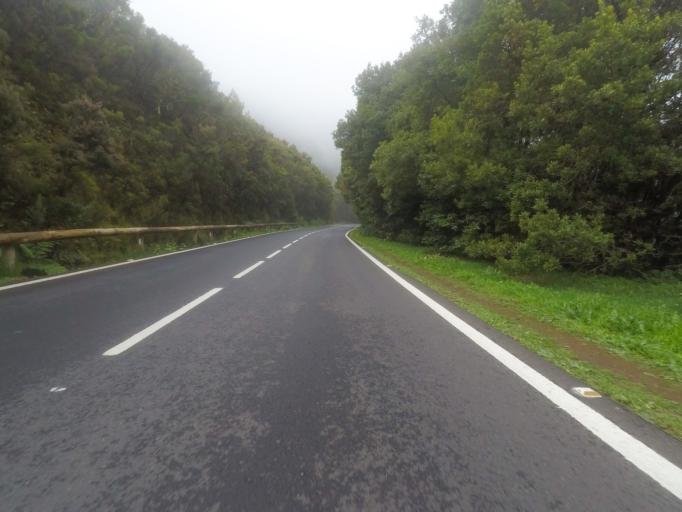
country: ES
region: Canary Islands
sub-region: Provincia de Santa Cruz de Tenerife
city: Alajero
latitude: 28.1119
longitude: -17.2407
